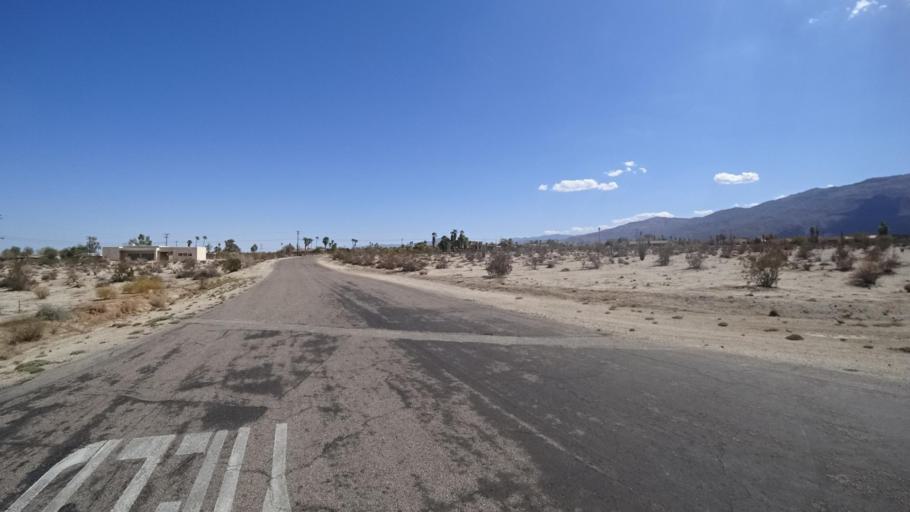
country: US
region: California
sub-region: San Diego County
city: Borrego Springs
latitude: 33.2367
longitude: -116.3823
